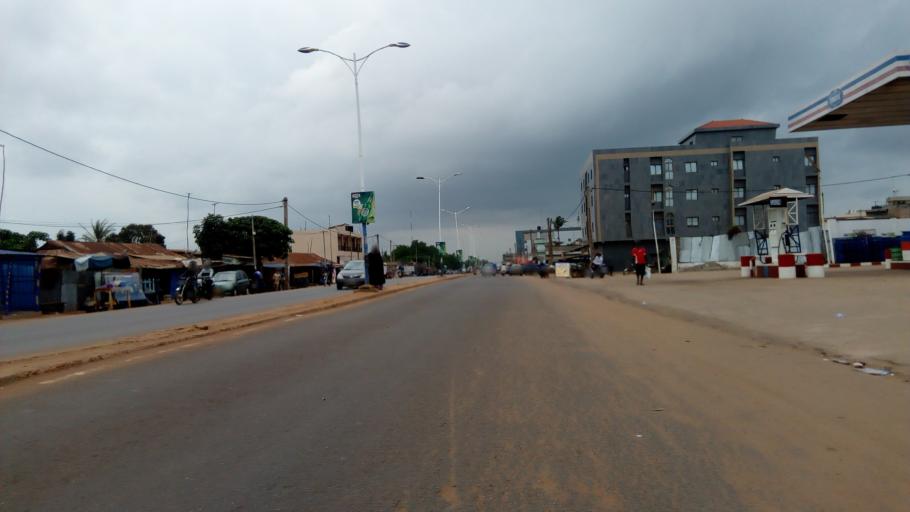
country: TG
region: Maritime
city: Lome
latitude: 6.2281
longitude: 1.2110
